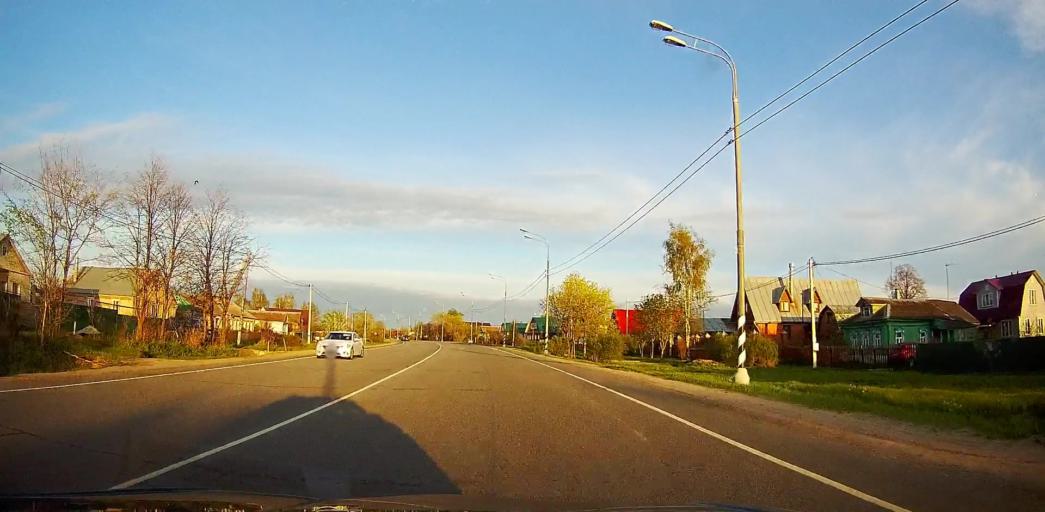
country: RU
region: Moskovskaya
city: Troitskoye
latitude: 55.2259
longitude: 38.5610
